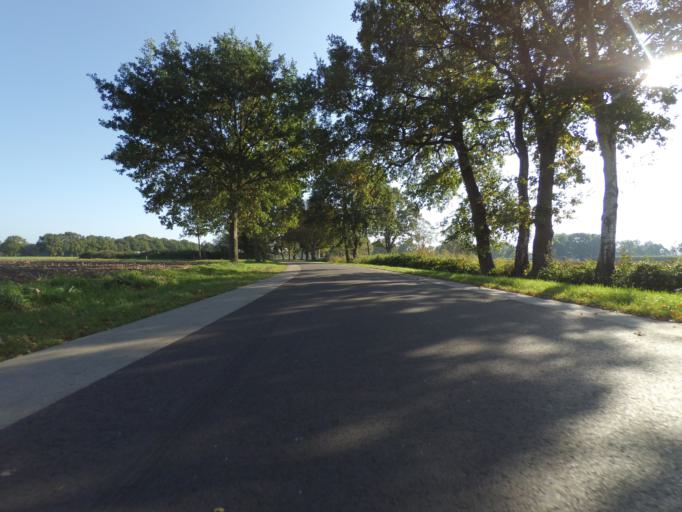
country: NL
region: Gelderland
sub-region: Gemeente Ede
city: Wekerom
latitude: 52.1496
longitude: 5.7205
